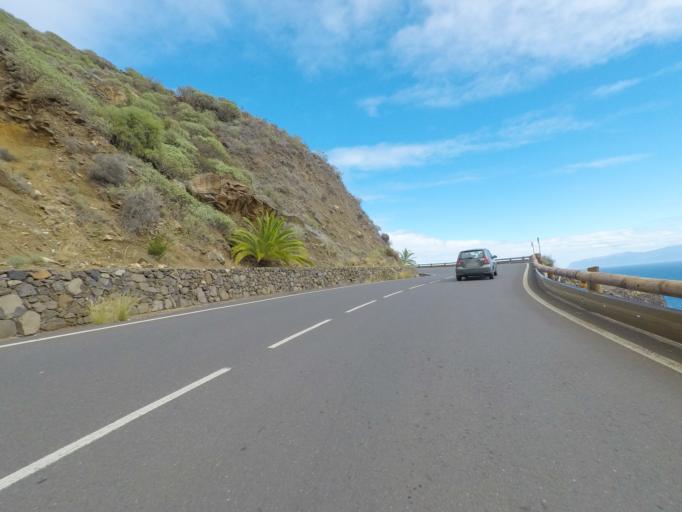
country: ES
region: Canary Islands
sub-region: Provincia de Santa Cruz de Tenerife
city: Agulo
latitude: 28.1817
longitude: -17.1875
